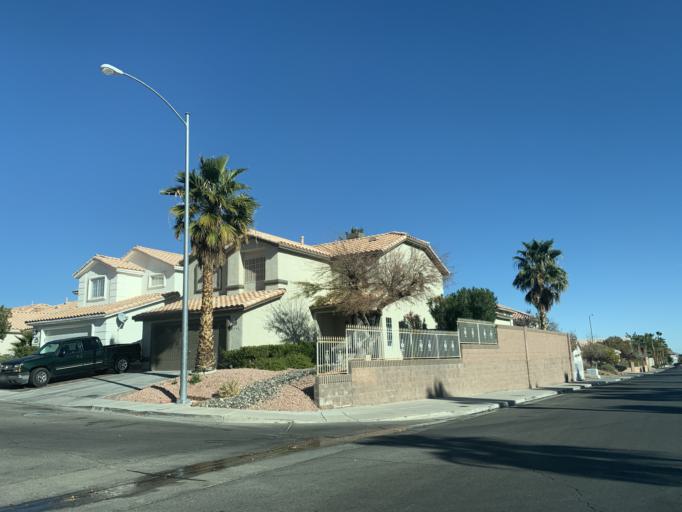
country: US
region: Nevada
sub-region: Clark County
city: Summerlin South
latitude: 36.1206
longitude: -115.3009
